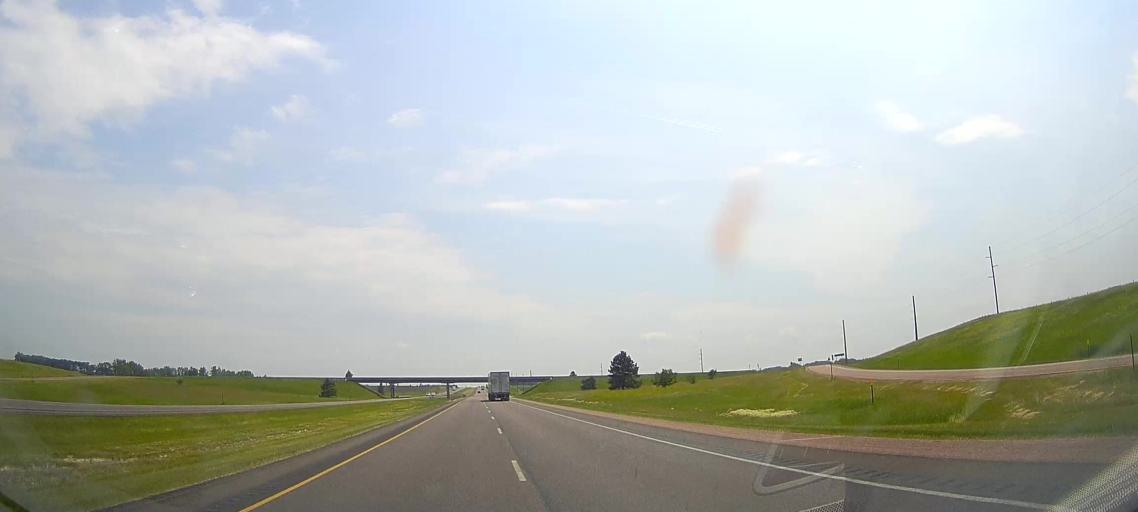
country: US
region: South Dakota
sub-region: Union County
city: Beresford
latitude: 43.1726
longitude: -96.7960
